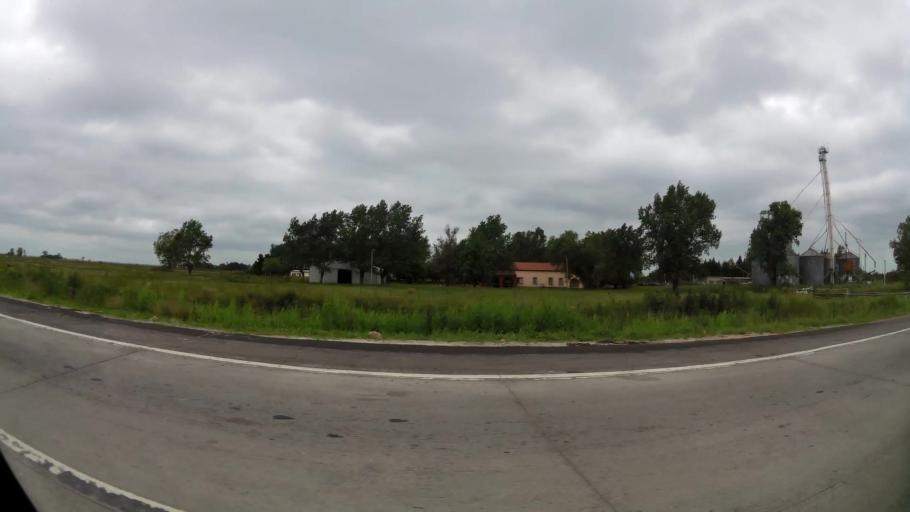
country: AR
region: Buenos Aires
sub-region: Partido de San Vicente
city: San Vicente
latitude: -35.0388
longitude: -58.4008
